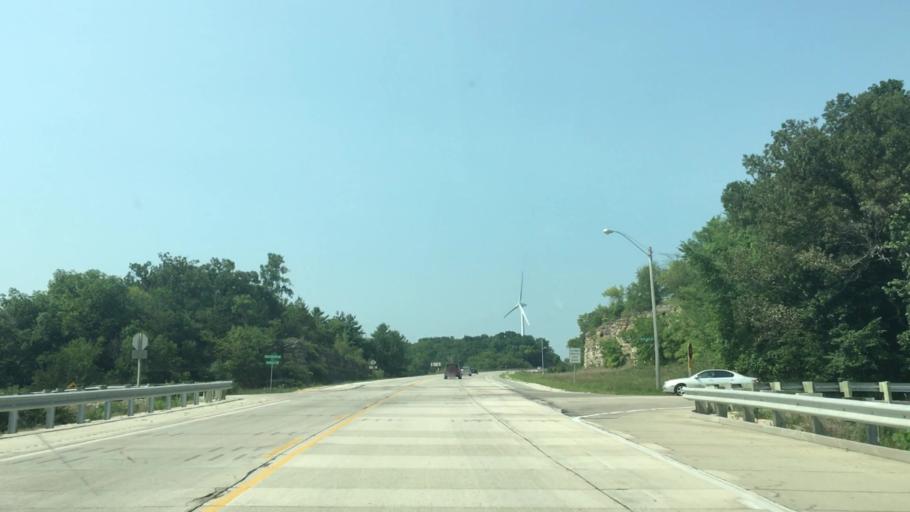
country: US
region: Iowa
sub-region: Winneshiek County
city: Decorah
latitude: 43.2999
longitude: -91.8128
